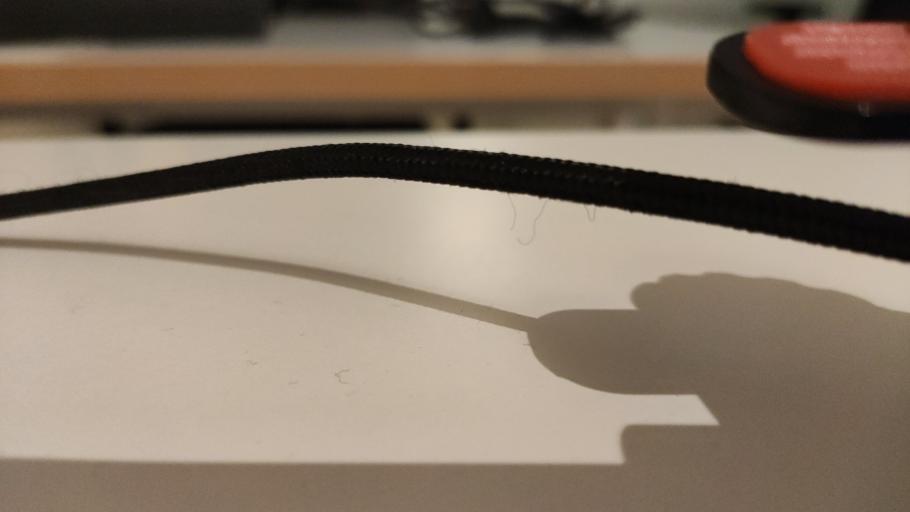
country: RU
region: Moskovskaya
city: Malino
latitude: 55.1114
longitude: 38.1588
